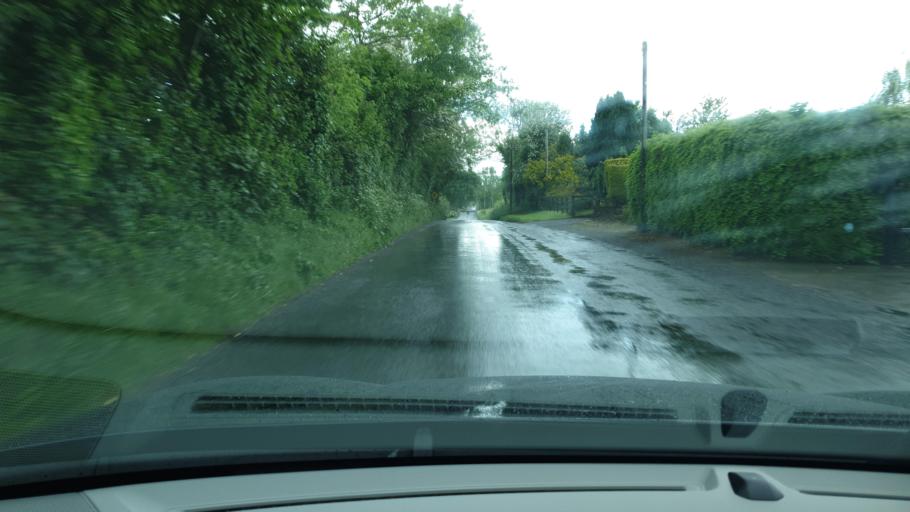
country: IE
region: Leinster
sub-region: Laois
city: Mountmellick
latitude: 53.1352
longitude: -7.3729
